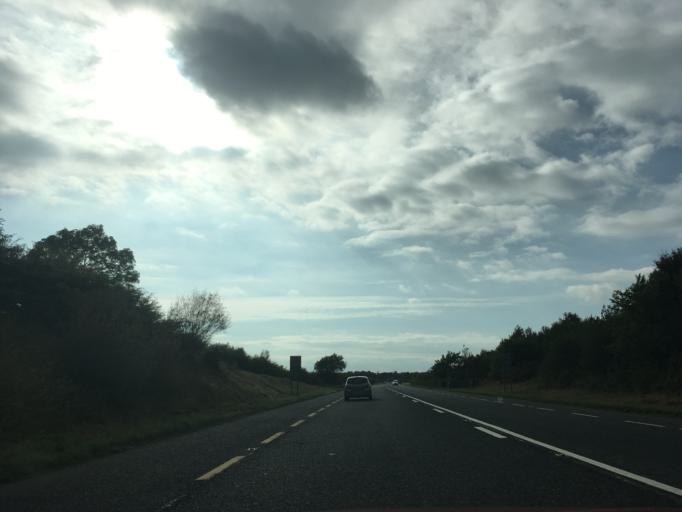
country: IE
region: Leinster
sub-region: Loch Garman
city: Loch Garman
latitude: 52.3484
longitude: -6.6215
